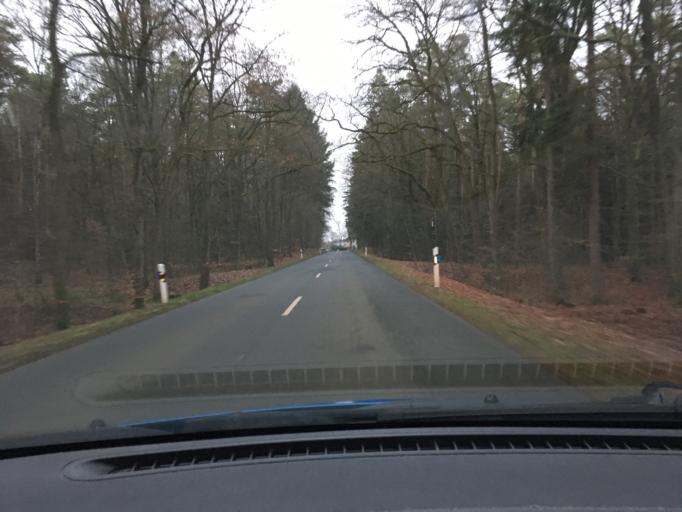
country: DE
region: Lower Saxony
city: Walsrode
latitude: 52.8459
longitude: 9.5909
